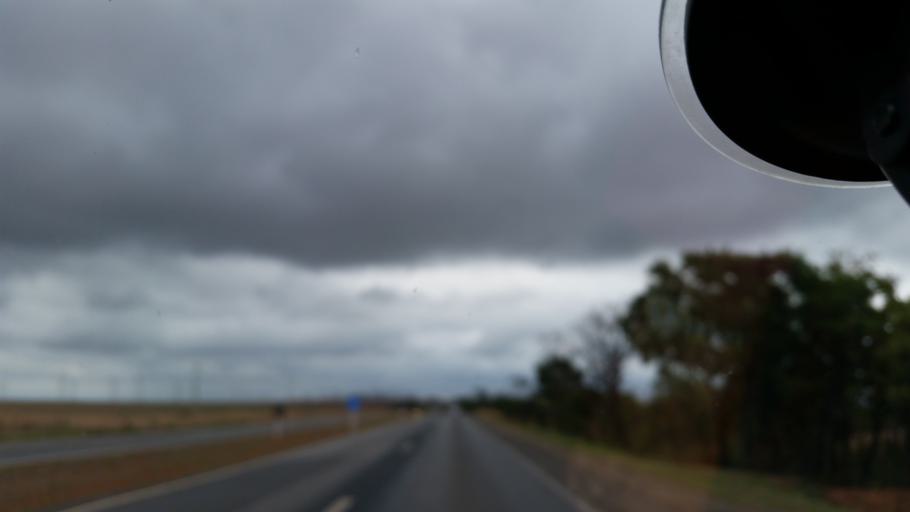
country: BR
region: Goias
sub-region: Luziania
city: Luziania
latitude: -16.3249
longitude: -47.8395
